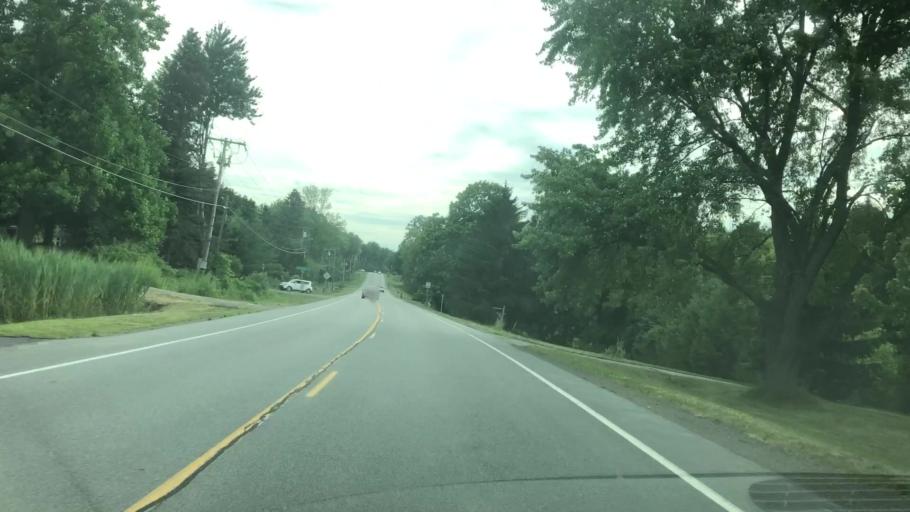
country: US
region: New York
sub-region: Monroe County
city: Fairport
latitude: 43.1343
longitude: -77.3652
